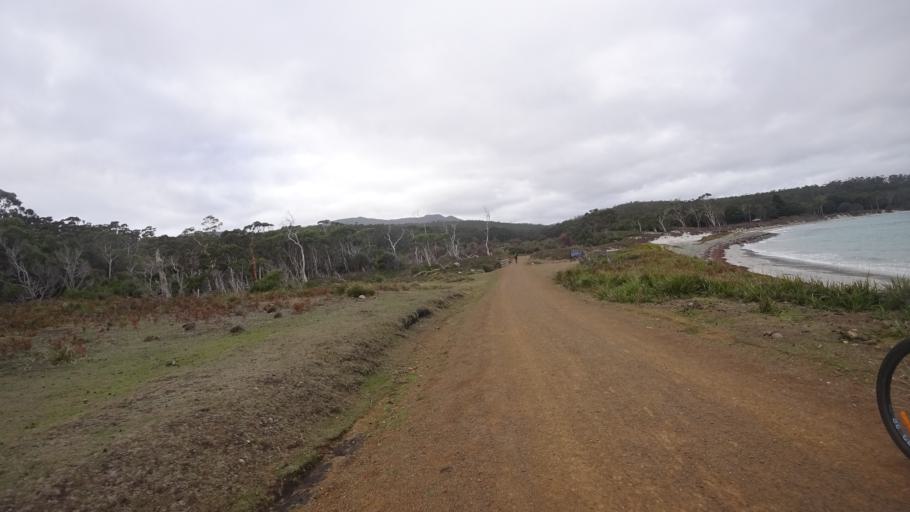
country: AU
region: Tasmania
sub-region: Sorell
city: Sorell
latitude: -42.5872
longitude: 148.0553
